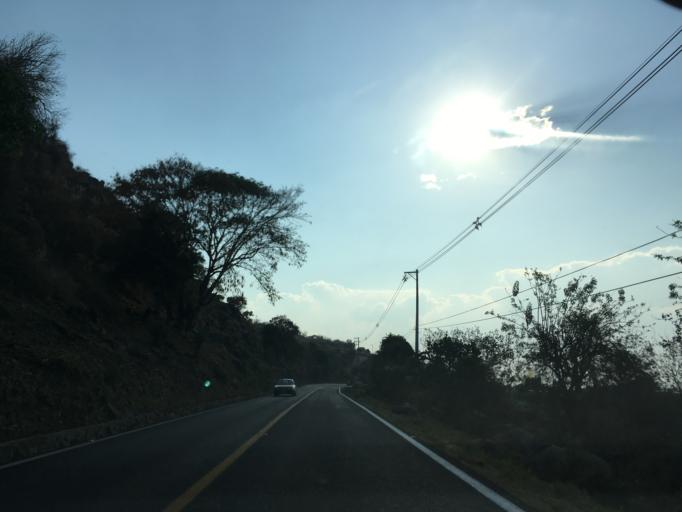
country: MX
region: Michoacan
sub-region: Indaparapeo
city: Colonia de Guadalupe
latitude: 19.8066
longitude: -100.8738
